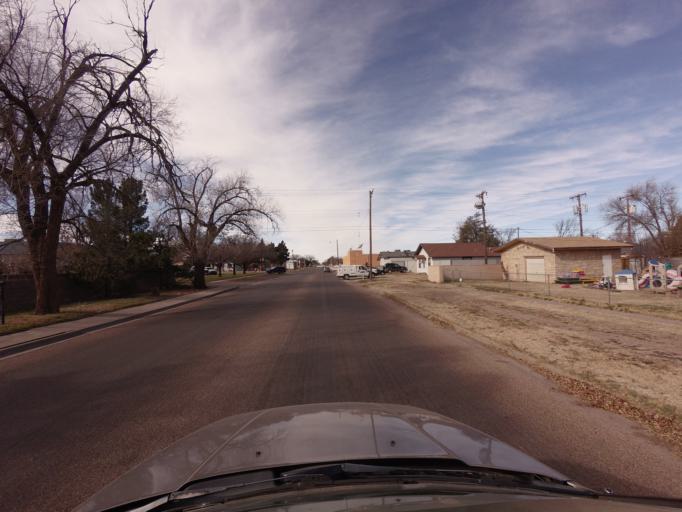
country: US
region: New Mexico
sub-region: Curry County
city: Clovis
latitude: 34.4079
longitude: -103.2031
